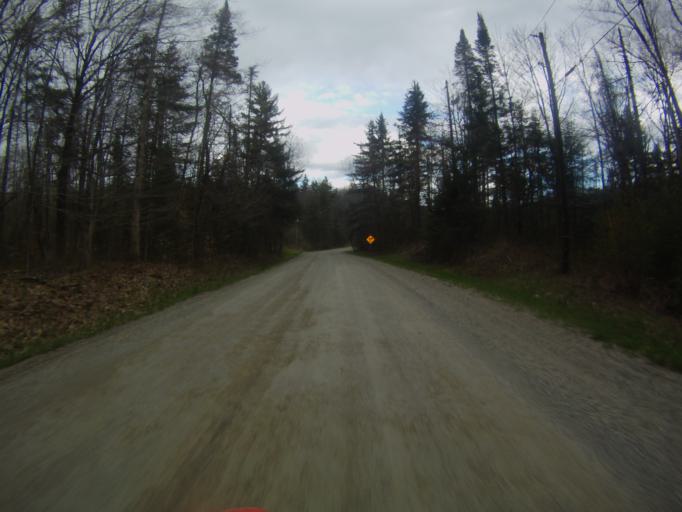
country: US
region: Vermont
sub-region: Addison County
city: Bristol
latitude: 44.0231
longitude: -73.0227
